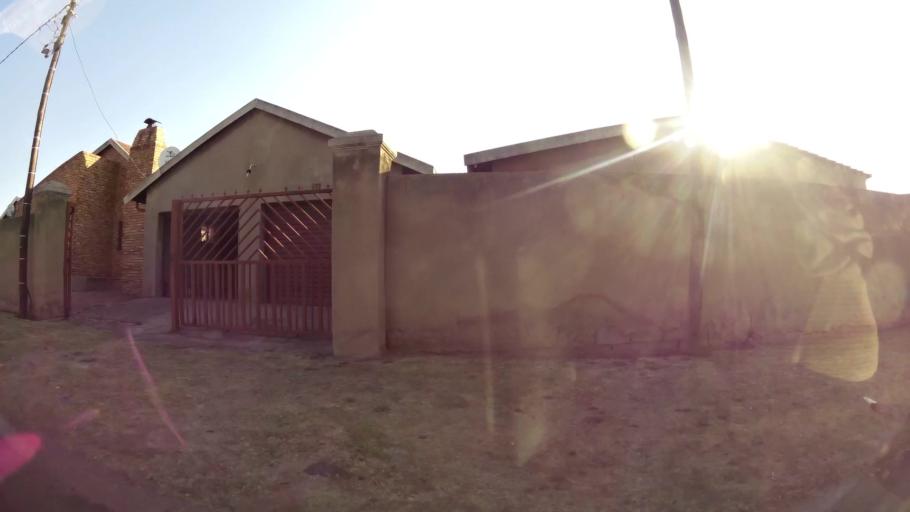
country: ZA
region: Gauteng
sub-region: City of Johannesburg Metropolitan Municipality
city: Soweto
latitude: -26.2646
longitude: 27.8760
